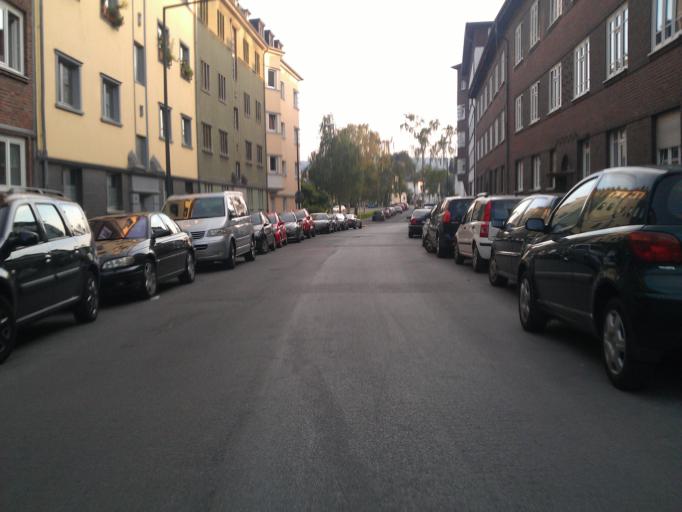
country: DE
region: North Rhine-Westphalia
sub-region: Regierungsbezirk Koln
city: Aachen
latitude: 50.7655
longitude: 6.0760
